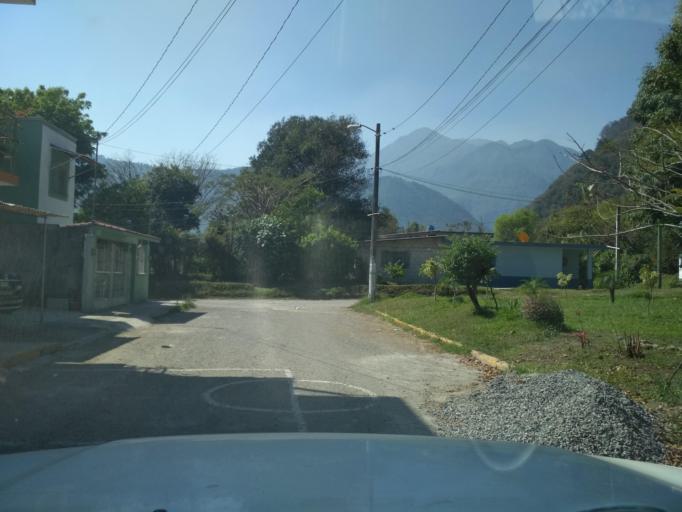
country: MX
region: Veracruz
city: Jalapilla
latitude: 18.8191
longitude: -97.0895
